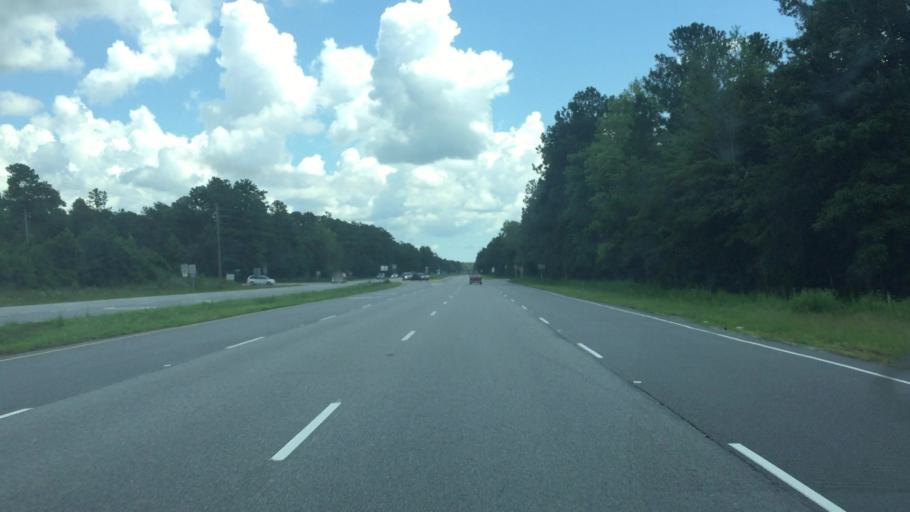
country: US
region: South Carolina
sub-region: Horry County
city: Loris
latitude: 34.0406
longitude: -78.8212
